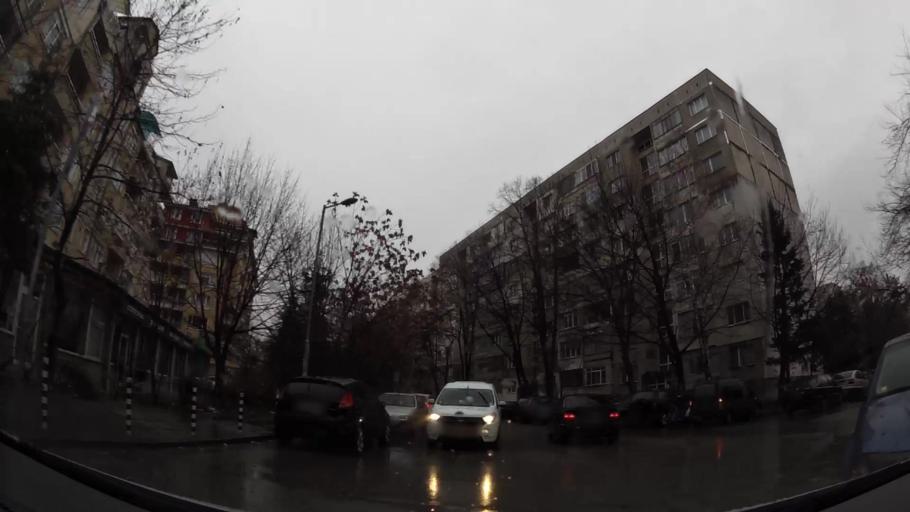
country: BG
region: Sofia-Capital
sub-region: Stolichna Obshtina
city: Sofia
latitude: 42.6537
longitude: 23.3766
